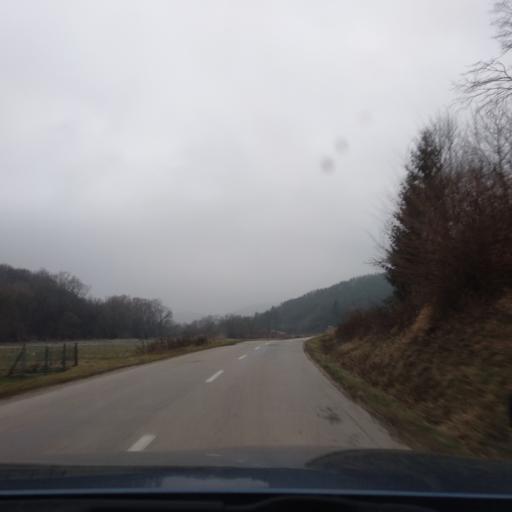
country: SK
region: Nitriansky
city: Trencianske Teplice
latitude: 48.9018
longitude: 18.2624
